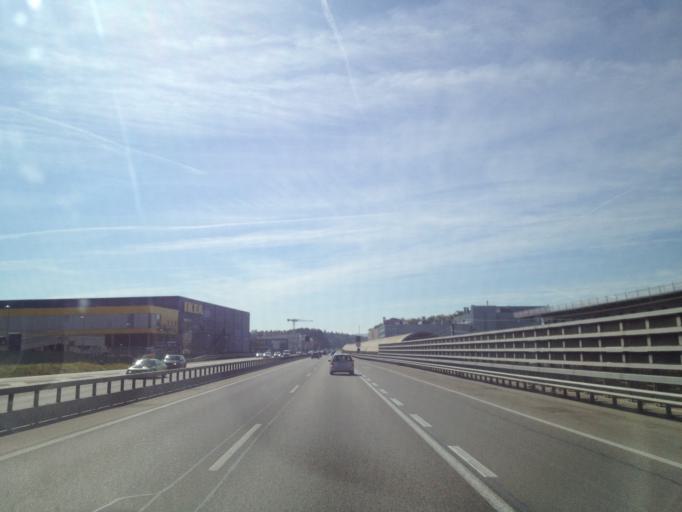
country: CH
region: Bern
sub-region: Emmental District
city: Kirchberg
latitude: 47.0770
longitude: 7.5701
